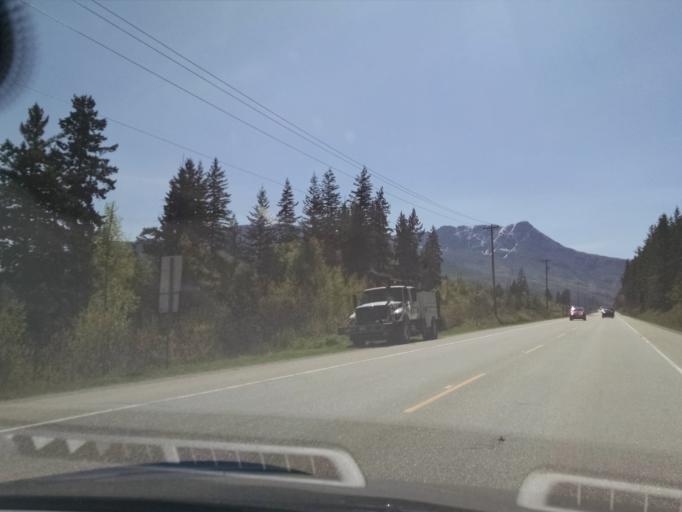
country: CA
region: British Columbia
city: Salmon Arm
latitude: 50.7215
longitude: -119.3172
